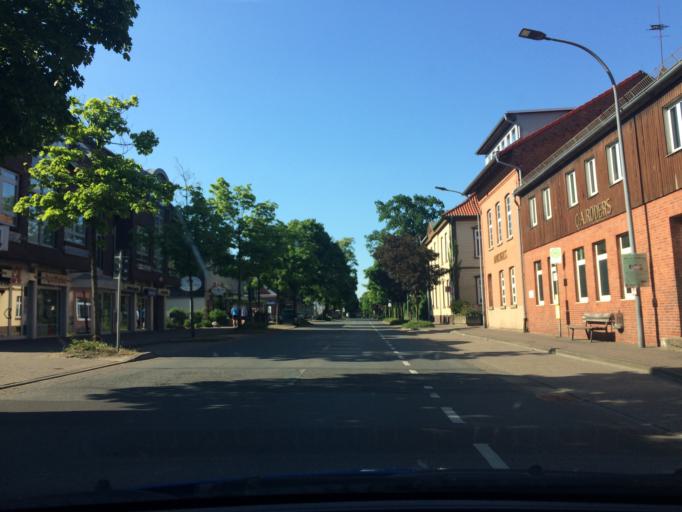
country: DE
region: Lower Saxony
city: Soltau
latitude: 52.9893
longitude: 9.8364
